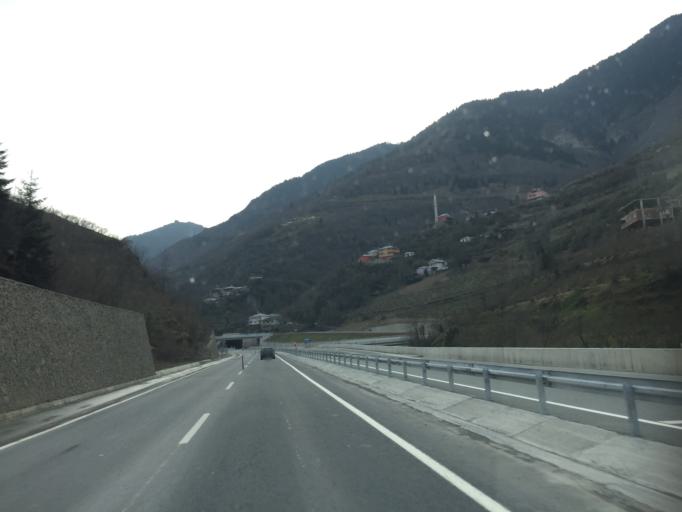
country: TR
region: Trabzon
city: Macka
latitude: 40.7816
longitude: 39.5721
